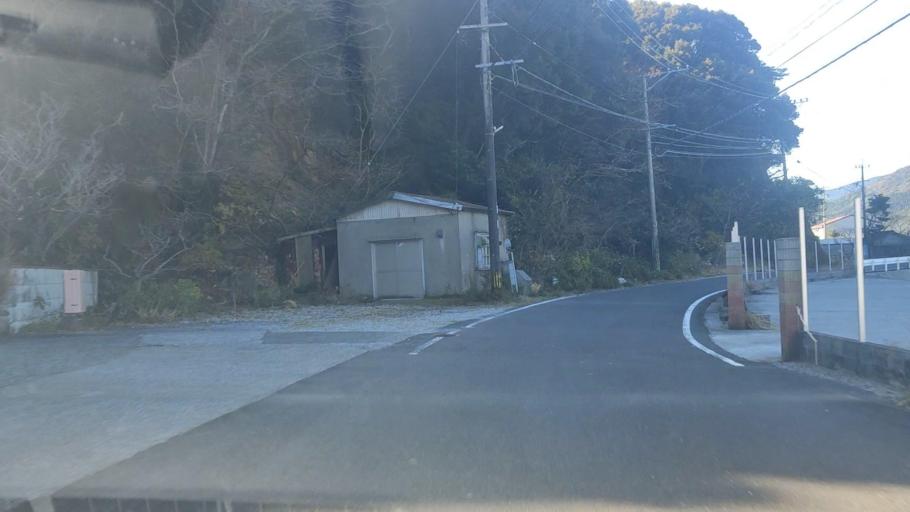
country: JP
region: Oita
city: Saiki
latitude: 32.7969
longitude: 131.8981
